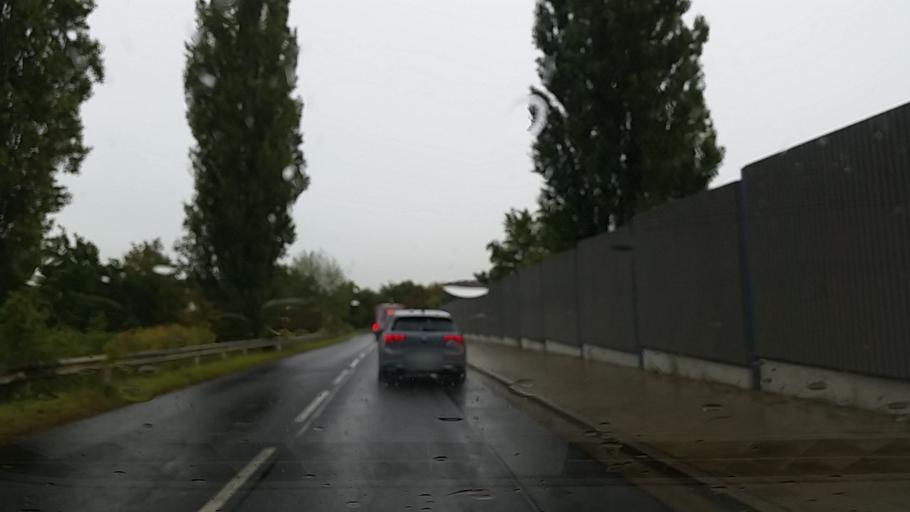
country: DE
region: Lower Saxony
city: Leiferde
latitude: 52.2073
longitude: 10.5059
